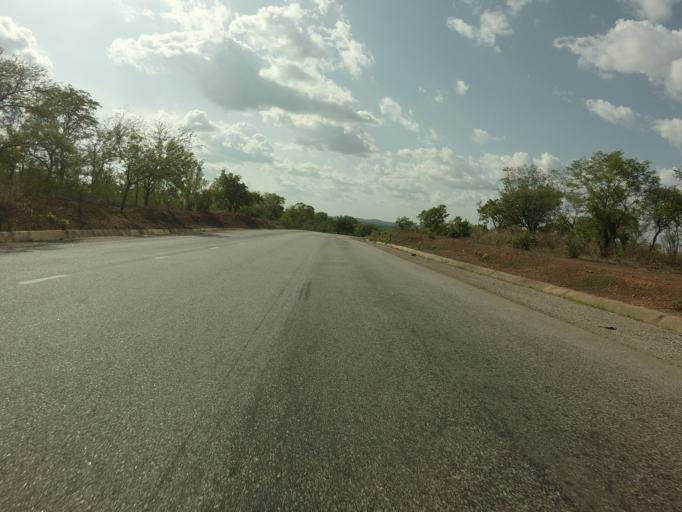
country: GH
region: Upper East
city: Bolgatanga
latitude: 10.5522
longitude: -0.8297
